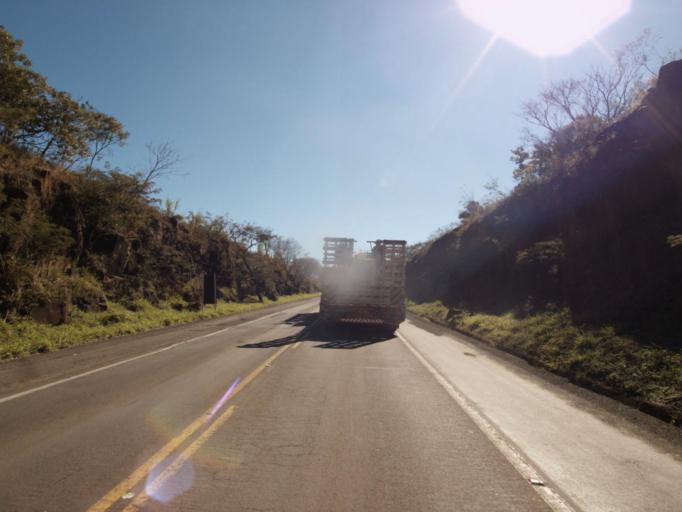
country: BR
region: Rio Grande do Sul
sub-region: Frederico Westphalen
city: Frederico Westphalen
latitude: -26.8114
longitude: -53.4376
